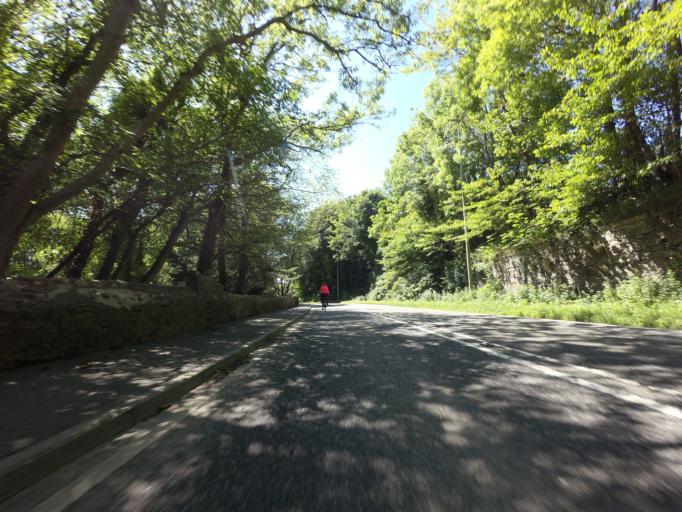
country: GB
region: Scotland
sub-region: Aberdeenshire
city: Macduff
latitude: 57.6603
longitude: -2.5036
